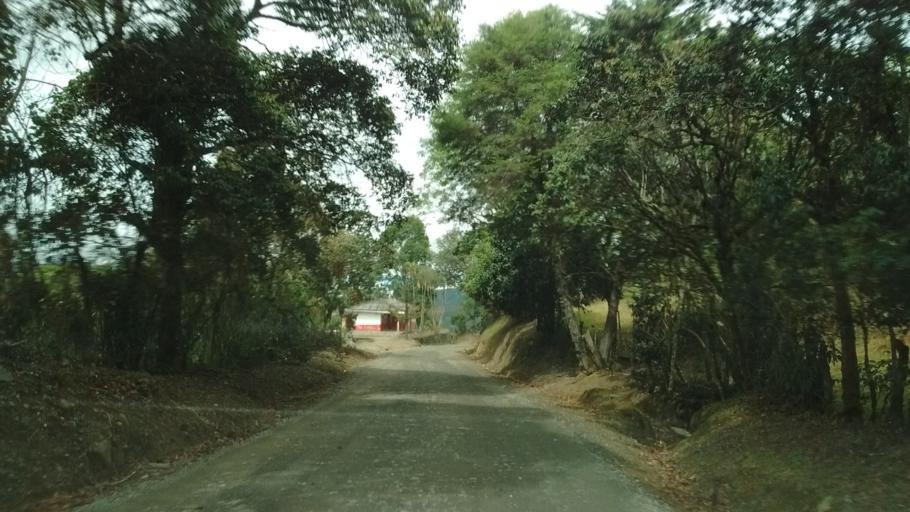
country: CO
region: Cauca
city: Almaguer
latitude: 1.8529
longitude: -76.9563
